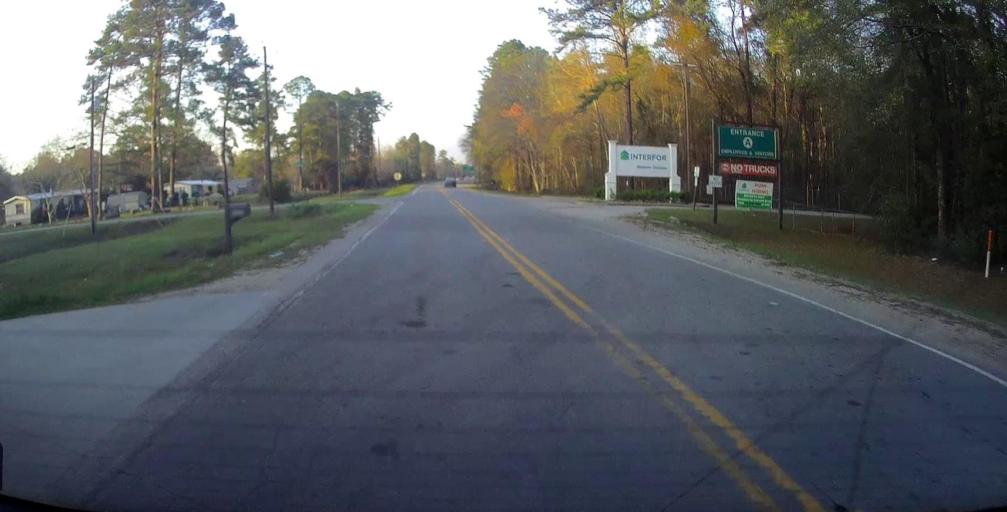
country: US
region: Georgia
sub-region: Chatham County
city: Bloomingdale
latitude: 32.1446
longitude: -81.3905
